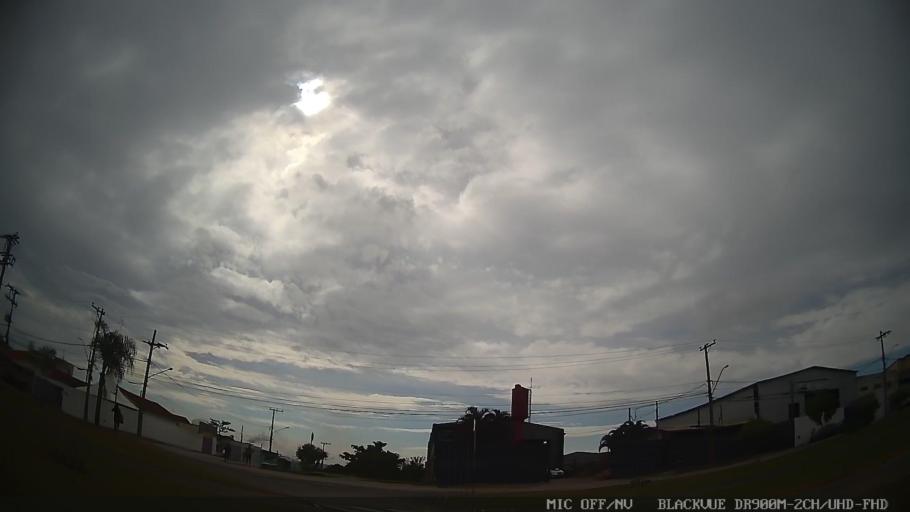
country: BR
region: Sao Paulo
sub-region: Salto
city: Salto
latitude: -23.2146
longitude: -47.2799
